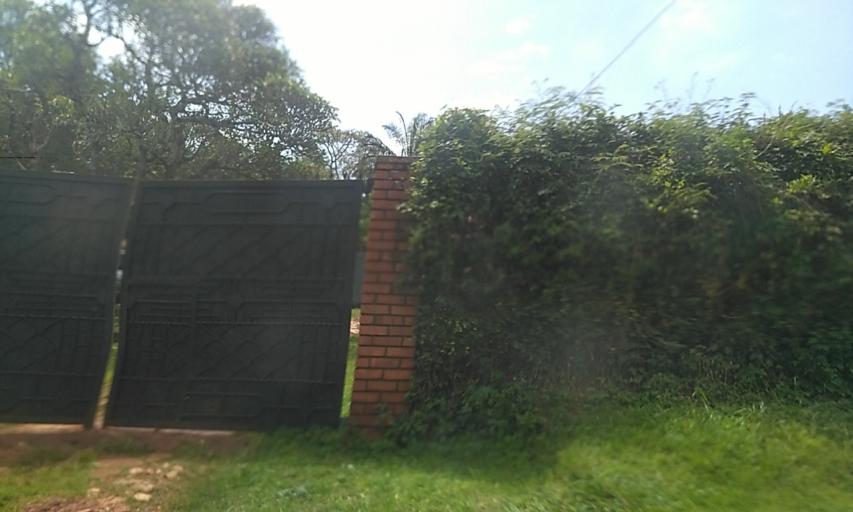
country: UG
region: Central Region
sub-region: Kampala District
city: Kampala
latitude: 0.3313
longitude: 32.6012
